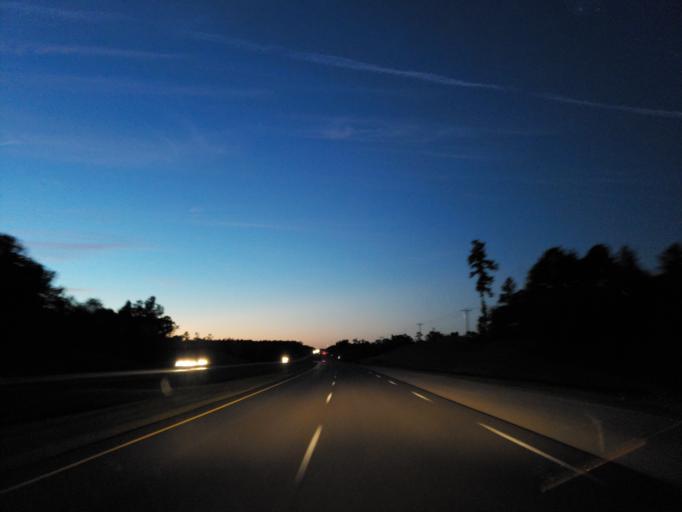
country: US
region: Mississippi
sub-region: Clarke County
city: Quitman
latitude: 32.0652
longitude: -88.6811
